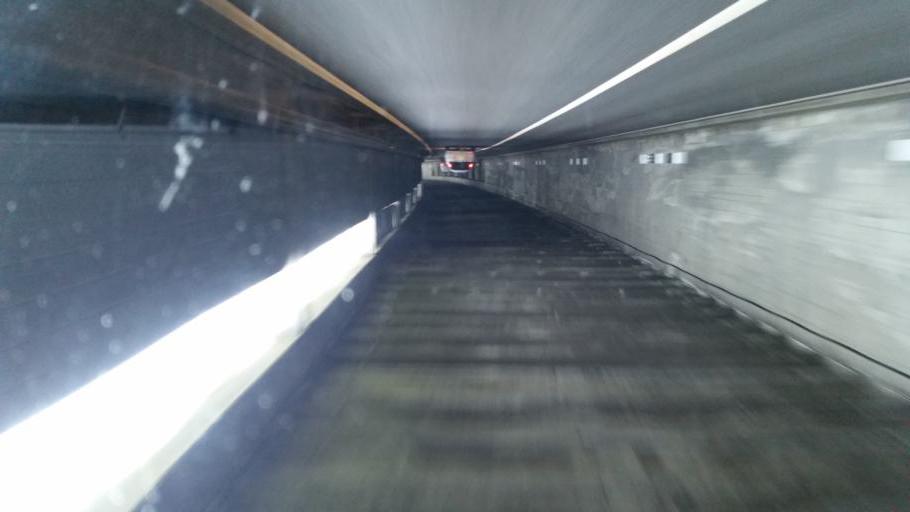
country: IT
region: Aosta Valley
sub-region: Valle d'Aosta
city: Saint-Oyen
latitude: 45.9059
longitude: 7.2009
